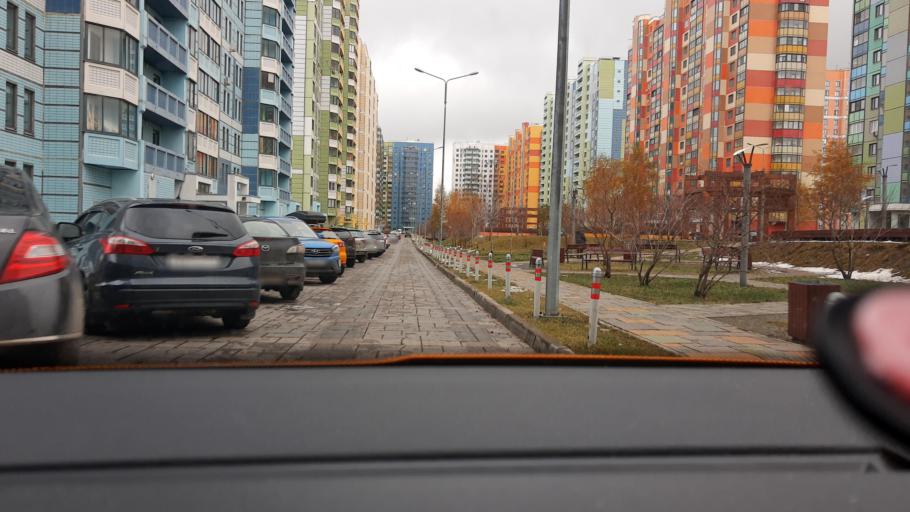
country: RU
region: Moscow
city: Businovo
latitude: 55.8772
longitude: 37.5054
